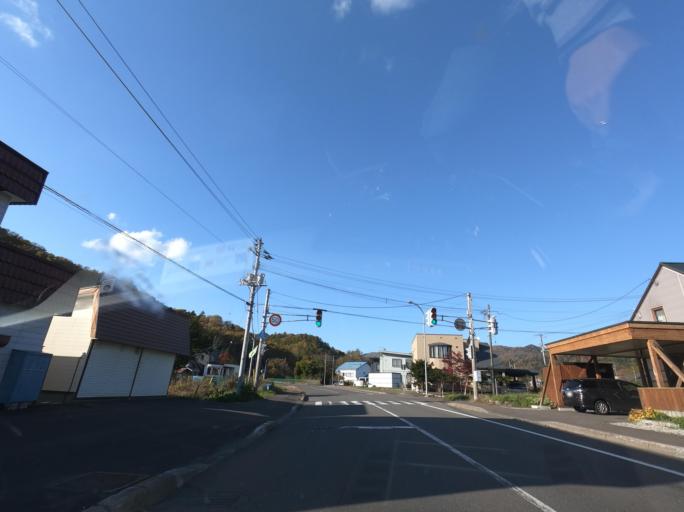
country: JP
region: Hokkaido
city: Iwamizawa
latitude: 42.9982
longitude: 142.0062
